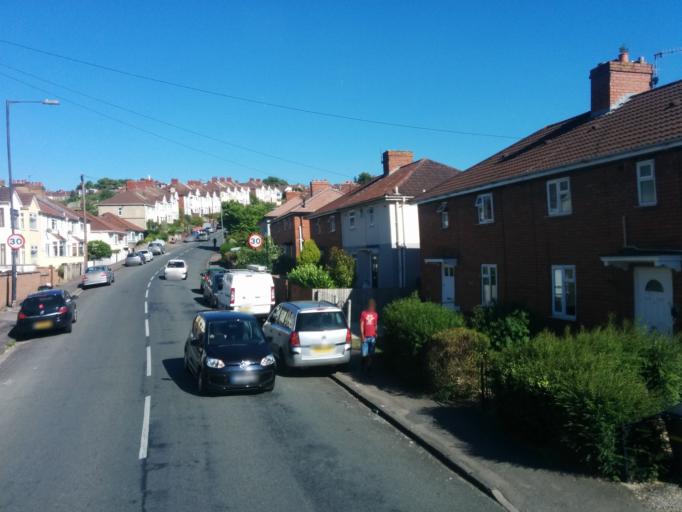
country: GB
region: England
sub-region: Bristol
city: Bristol
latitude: 51.4369
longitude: -2.5836
